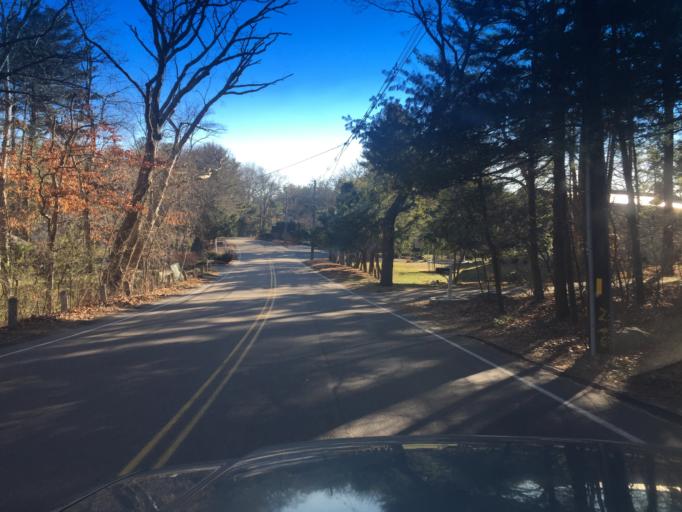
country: US
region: Massachusetts
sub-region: Middlesex County
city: Holliston
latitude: 42.1966
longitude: -71.4010
